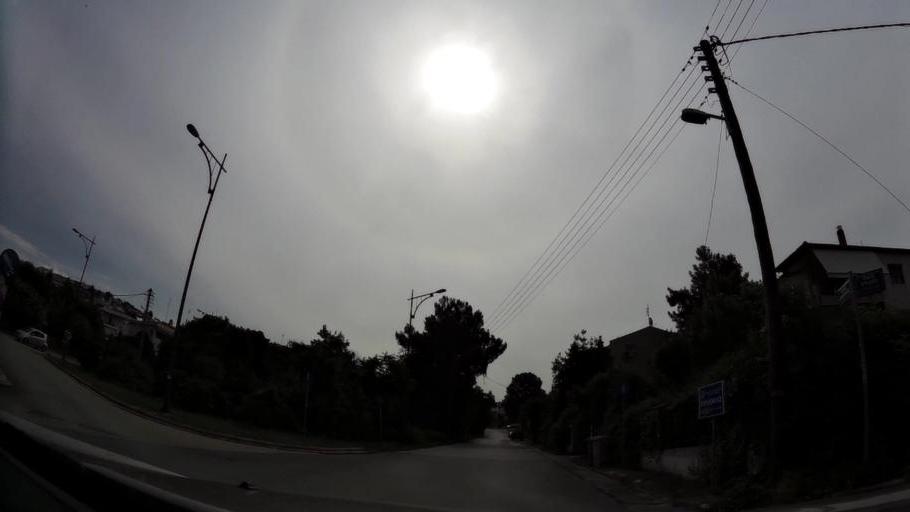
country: GR
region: Central Macedonia
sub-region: Nomos Thessalonikis
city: Panorama
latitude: 40.5824
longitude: 23.0220
